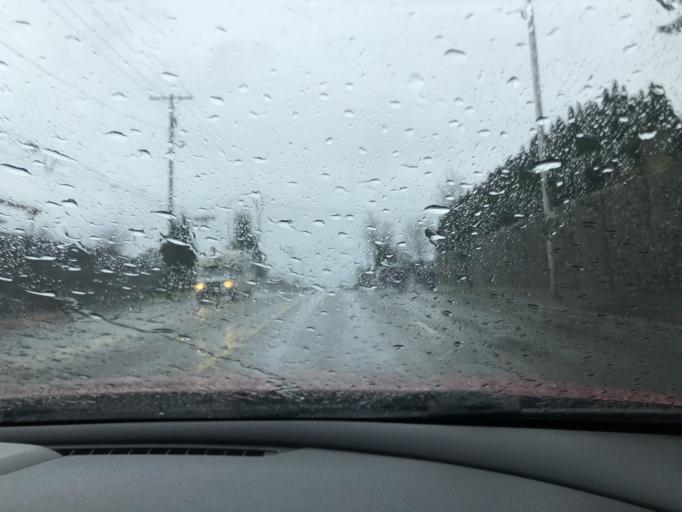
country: US
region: Washington
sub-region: Pierce County
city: Fircrest
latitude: 47.2428
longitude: -122.4870
